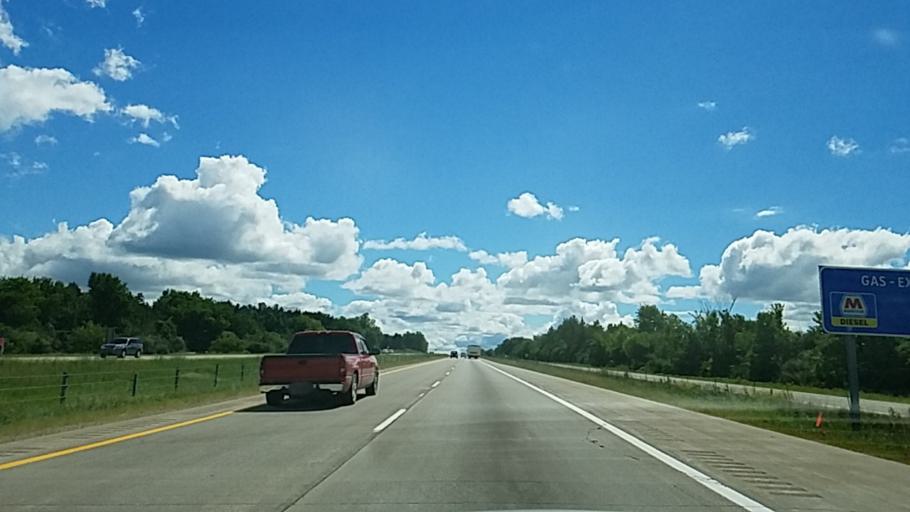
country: US
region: Michigan
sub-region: Genesee County
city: Linden
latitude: 42.7476
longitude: -83.7646
